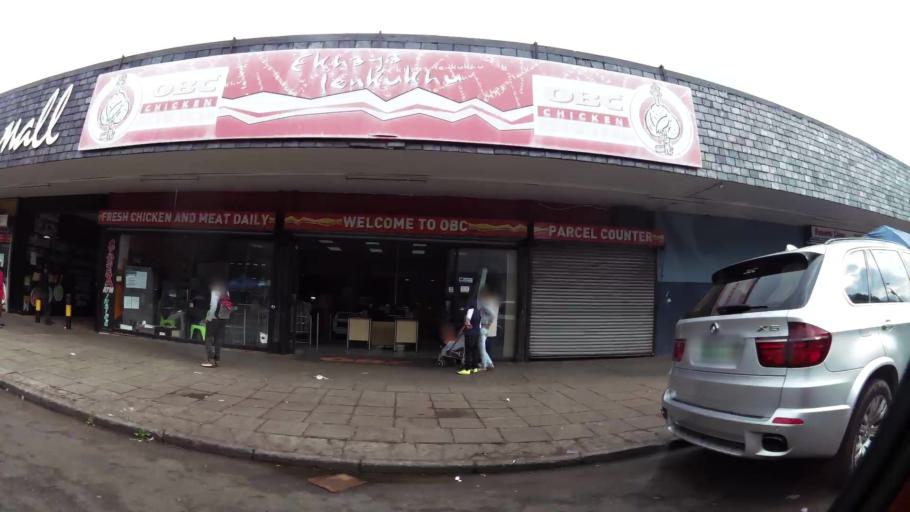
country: ZA
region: Gauteng
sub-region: Sedibeng District Municipality
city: Vanderbijlpark
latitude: -26.6980
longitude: 27.8376
